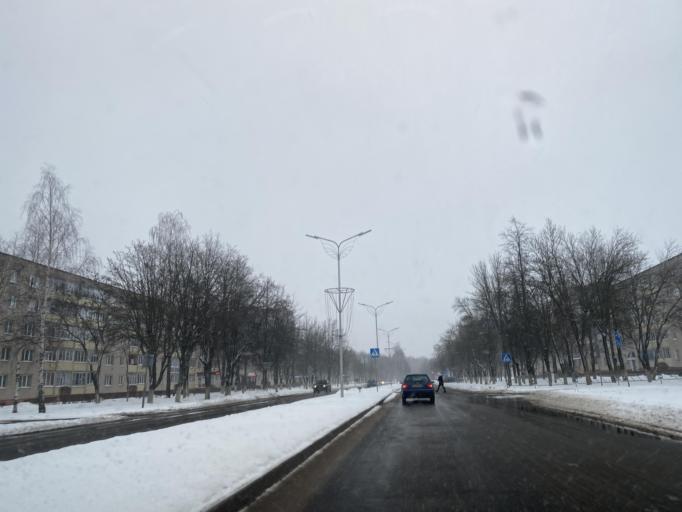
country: BY
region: Minsk
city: Horad Zhodzina
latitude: 54.0933
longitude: 28.3082
